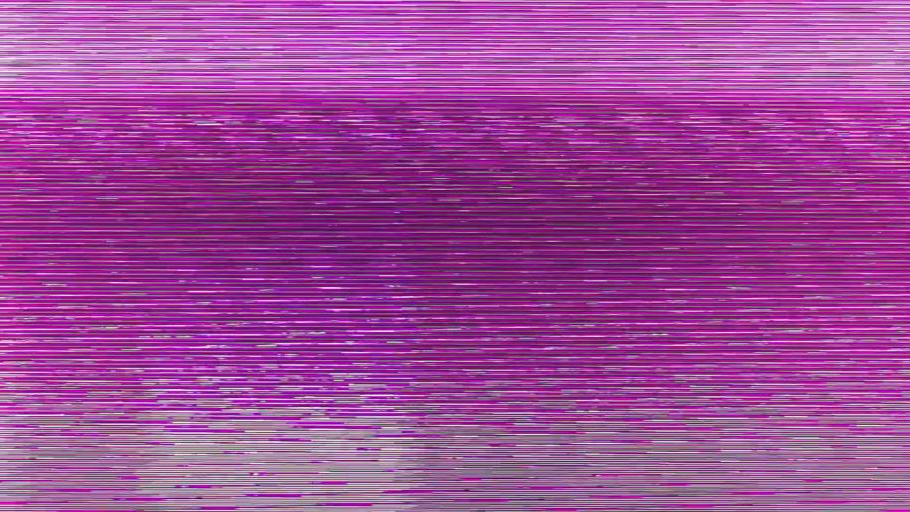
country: US
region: Michigan
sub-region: Washtenaw County
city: Ypsilanti
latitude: 42.2376
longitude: -83.6131
